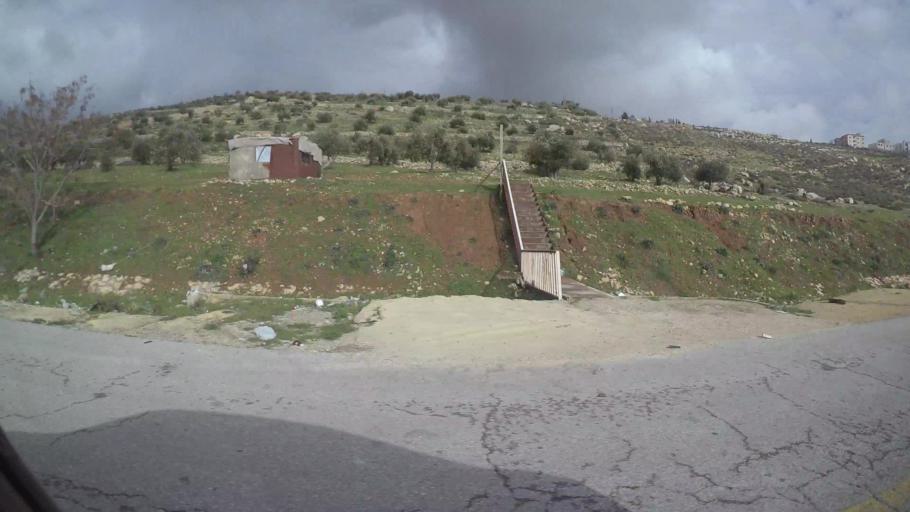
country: JO
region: Amman
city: Al Jubayhah
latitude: 32.0771
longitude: 35.8787
